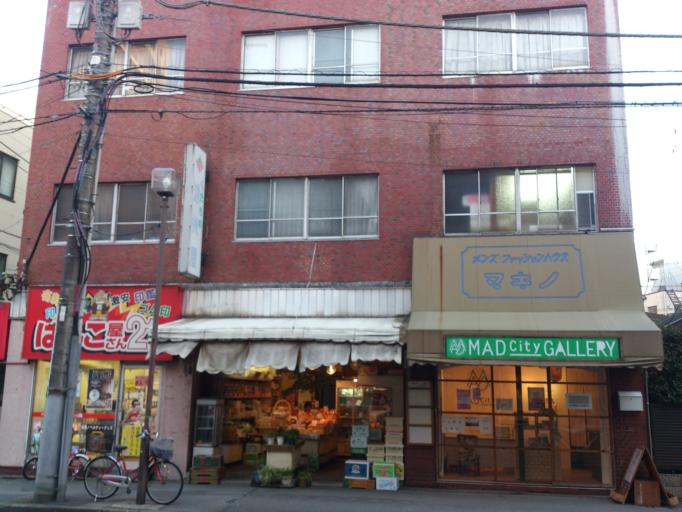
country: JP
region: Chiba
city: Matsudo
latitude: 35.7845
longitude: 139.8976
